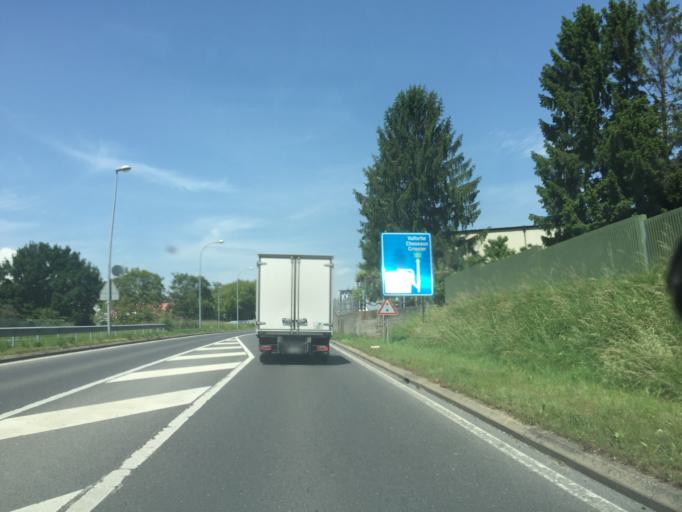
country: CH
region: Vaud
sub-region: Ouest Lausannois District
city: Crissier
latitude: 46.5492
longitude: 6.5754
